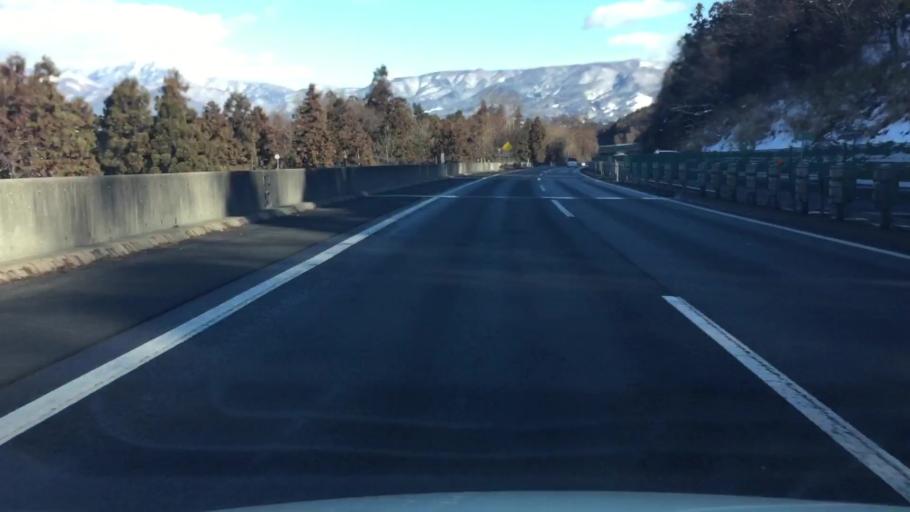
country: JP
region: Gunma
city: Numata
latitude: 36.6333
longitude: 139.0712
